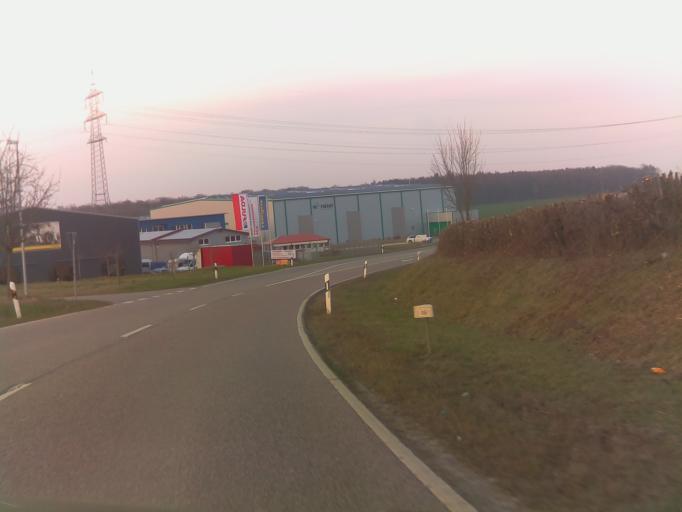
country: DE
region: Baden-Wuerttemberg
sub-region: Regierungsbezirk Stuttgart
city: Hemmingen
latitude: 48.8905
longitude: 9.0051
